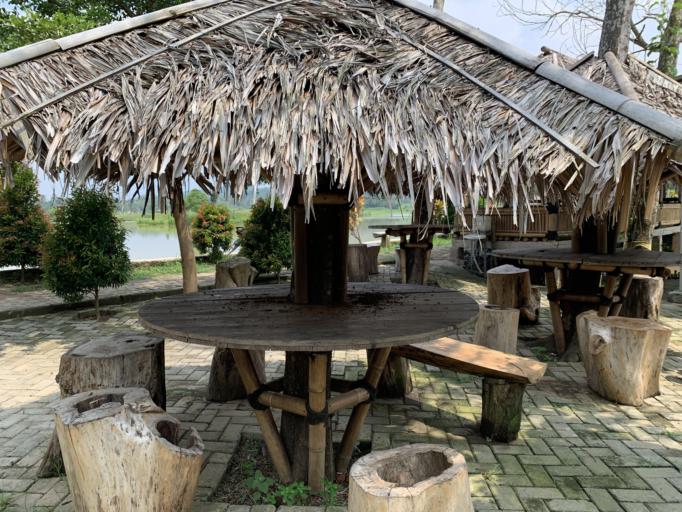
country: ID
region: West Java
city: Serpong
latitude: -6.3649
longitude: 106.5834
